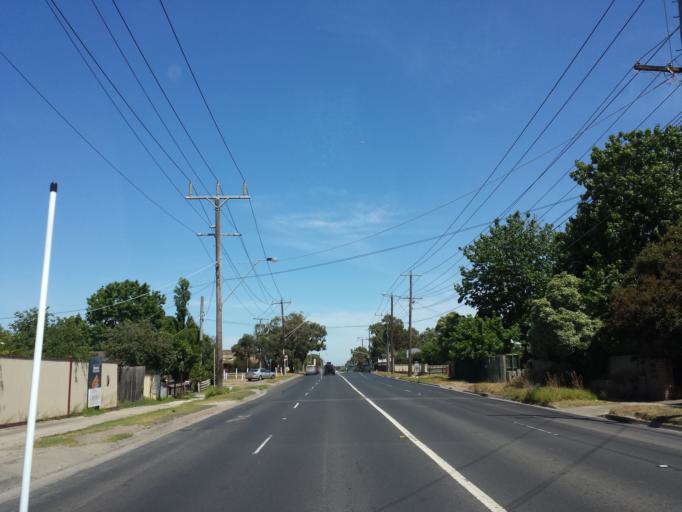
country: AU
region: Victoria
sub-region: Greater Dandenong
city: Springvale South
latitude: -37.9600
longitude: 145.1327
